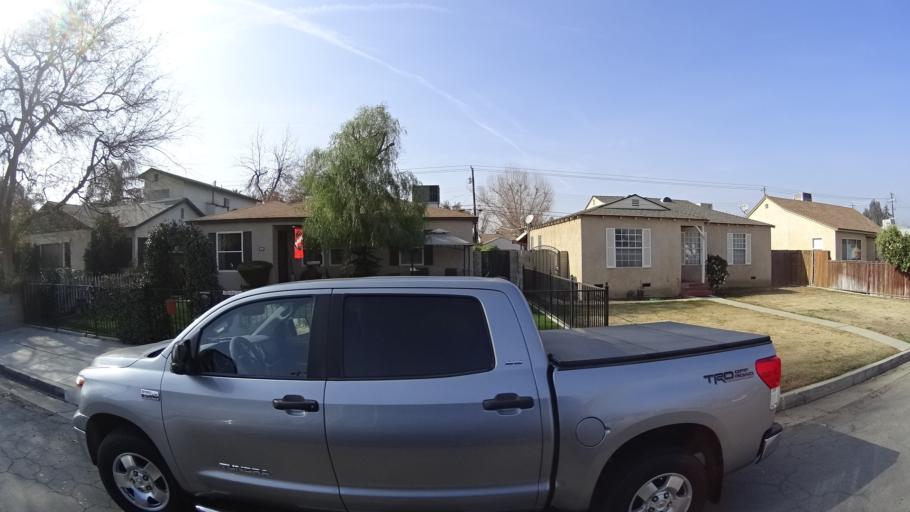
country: US
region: California
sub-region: Kern County
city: Bakersfield
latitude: 35.3604
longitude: -119.0351
